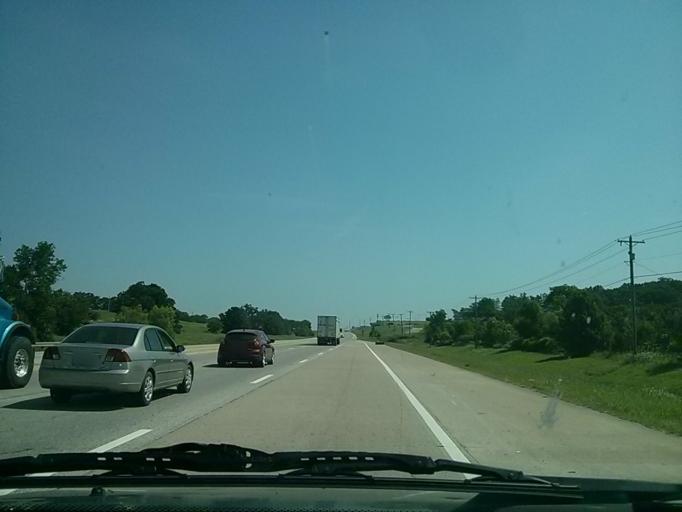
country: US
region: Oklahoma
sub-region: Creek County
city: Sapulpa
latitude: 36.0301
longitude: -96.0883
